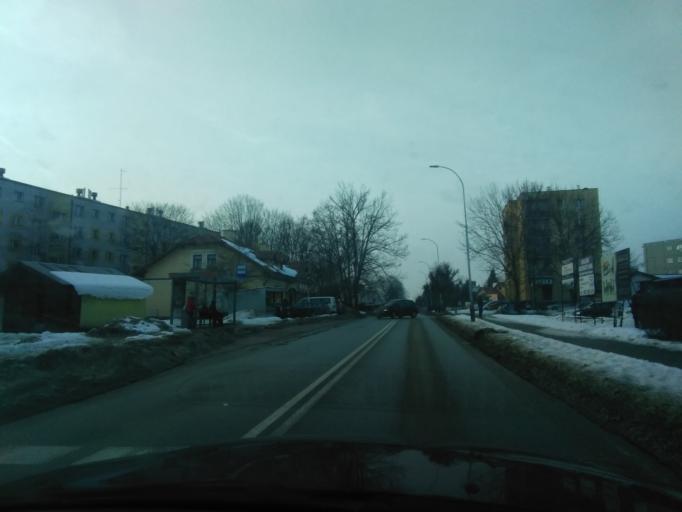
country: PL
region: Subcarpathian Voivodeship
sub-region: Krosno
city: Krosno
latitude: 49.6864
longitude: 21.7736
